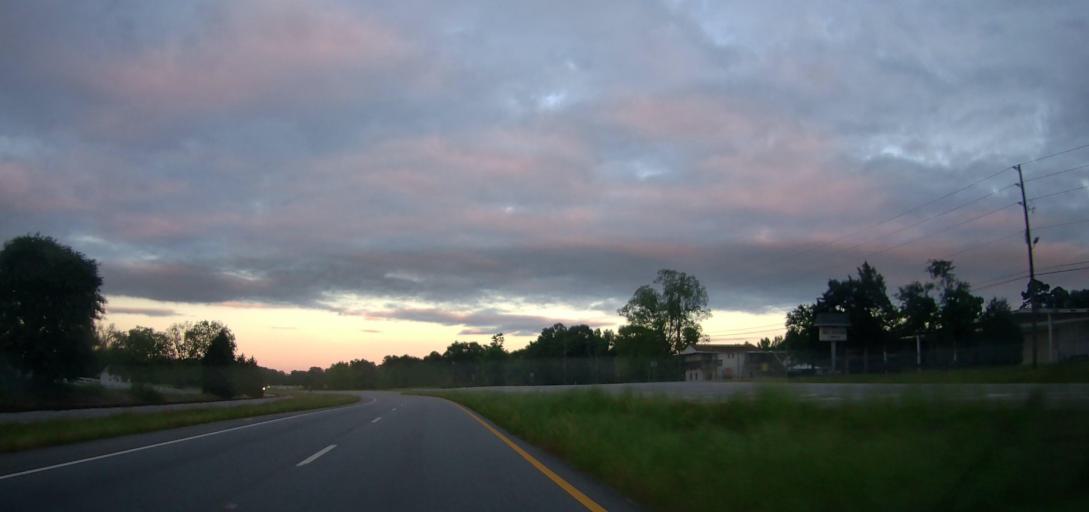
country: US
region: Georgia
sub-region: Clarke County
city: Country Club Estates
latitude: 34.0058
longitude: -83.4600
